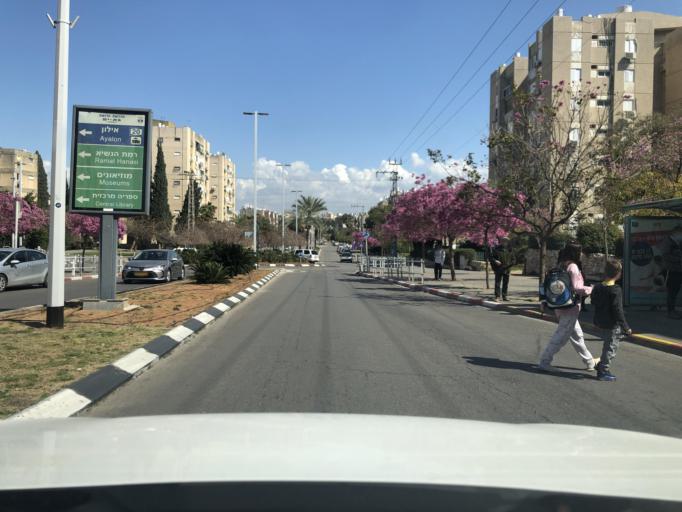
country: IL
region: Tel Aviv
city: Bat Yam
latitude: 32.0091
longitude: 34.7569
